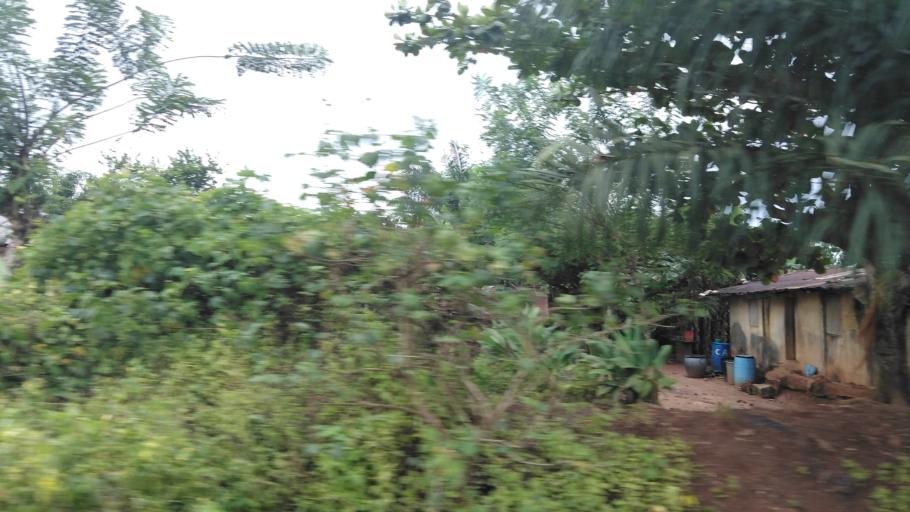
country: NG
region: Ogun
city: Abigi
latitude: 6.5964
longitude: 4.4955
